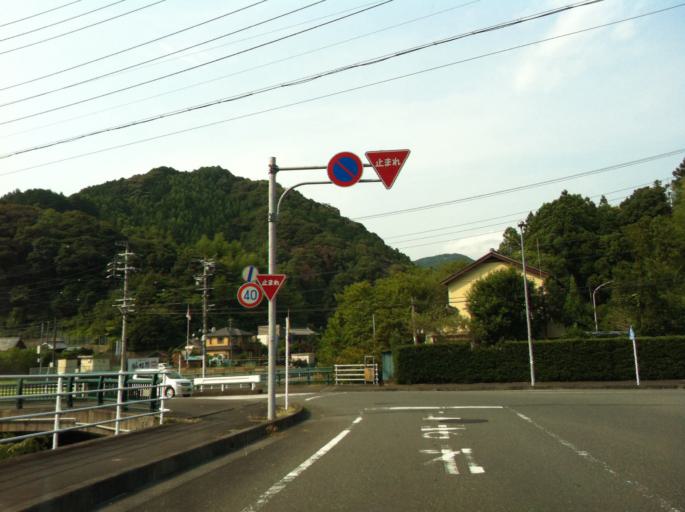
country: JP
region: Shizuoka
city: Fujieda
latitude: 34.9281
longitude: 138.2718
